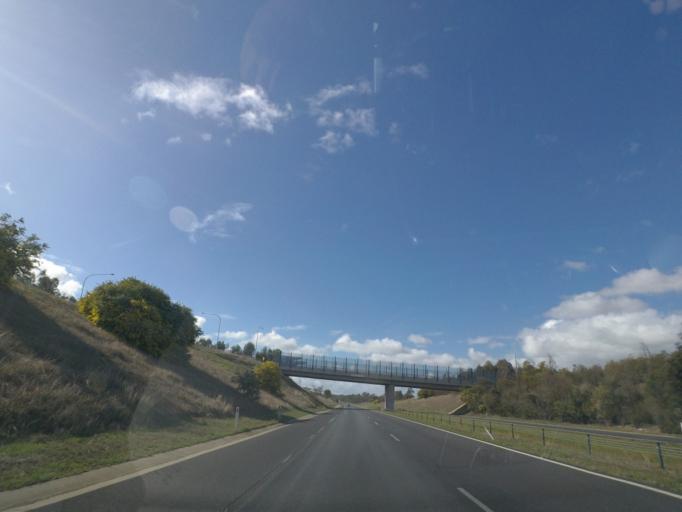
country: AU
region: New South Wales
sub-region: Albury Municipality
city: Lavington
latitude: -36.0530
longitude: 146.9580
